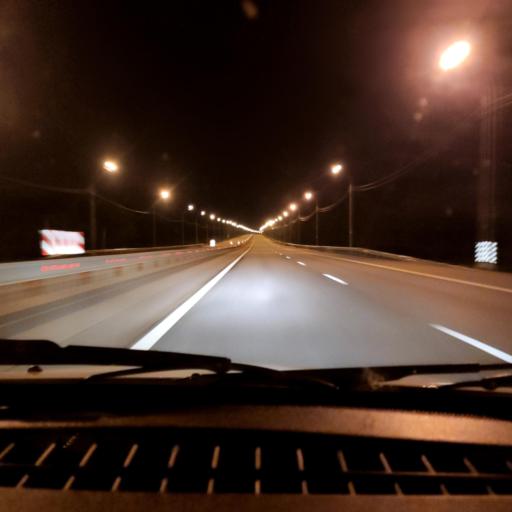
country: RU
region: Lipetsk
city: Zadonsk
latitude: 52.3348
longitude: 38.9896
